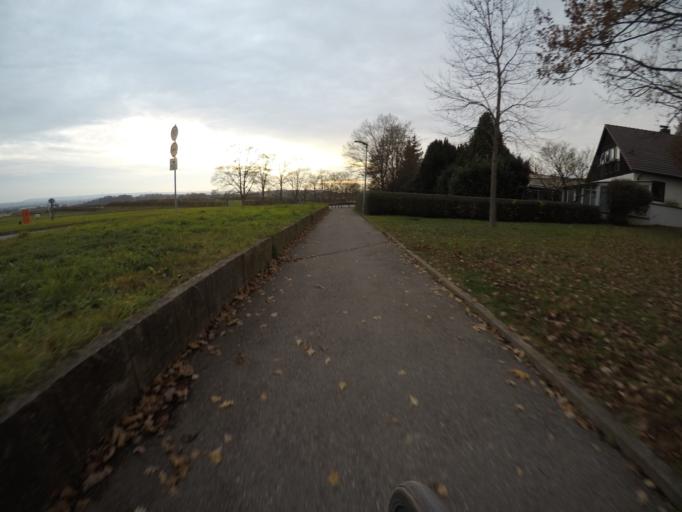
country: DE
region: Baden-Wuerttemberg
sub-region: Regierungsbezirk Stuttgart
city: Ostfildern
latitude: 48.7257
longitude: 9.2678
